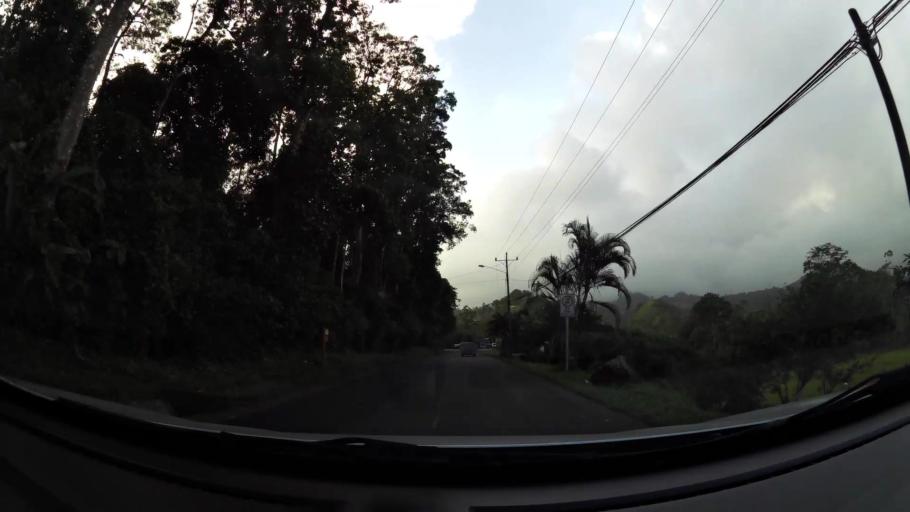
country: CR
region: Cartago
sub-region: Canton de Turrialba
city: La Suiza
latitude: 9.9584
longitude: -83.5689
